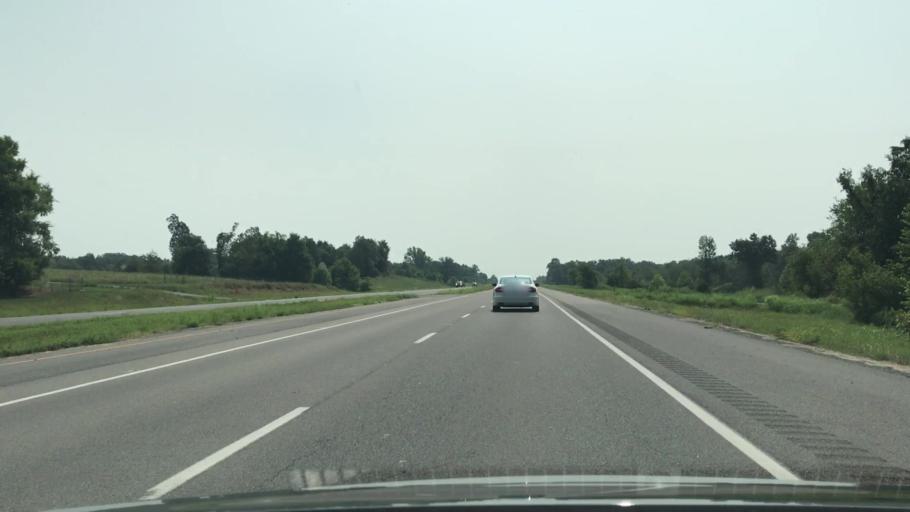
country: US
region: Kentucky
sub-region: Graves County
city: Mayfield
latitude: 36.6680
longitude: -88.4940
